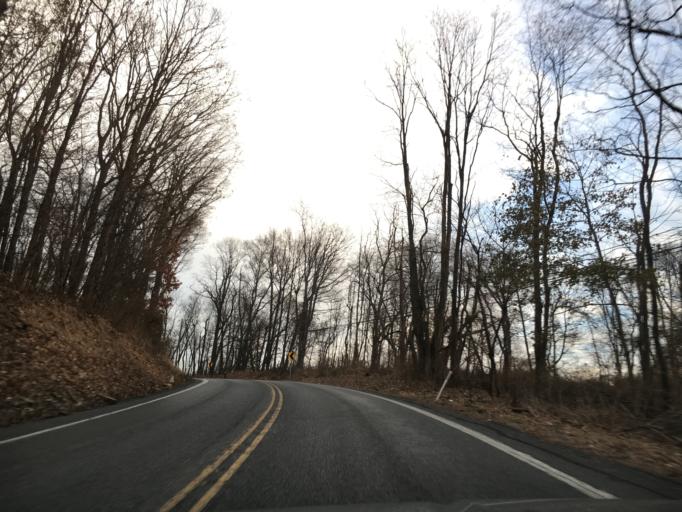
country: US
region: Pennsylvania
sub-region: Lehigh County
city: Slatington
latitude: 40.7197
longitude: -75.6084
